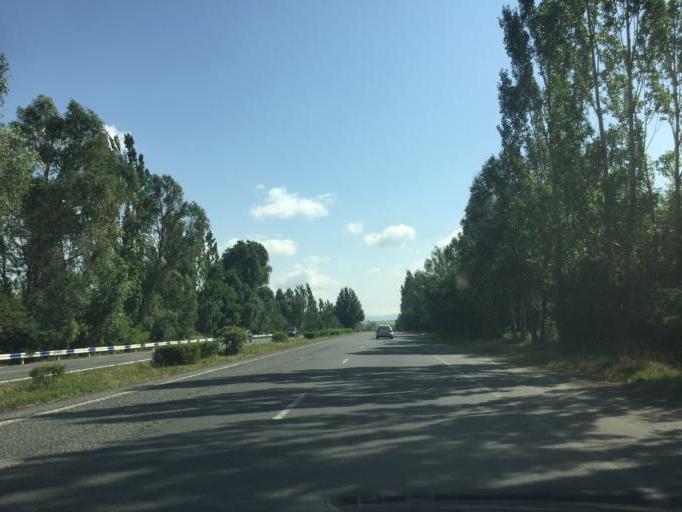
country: AM
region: Kotayk'i Marz
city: Hrazdan
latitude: 40.4789
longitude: 44.7571
